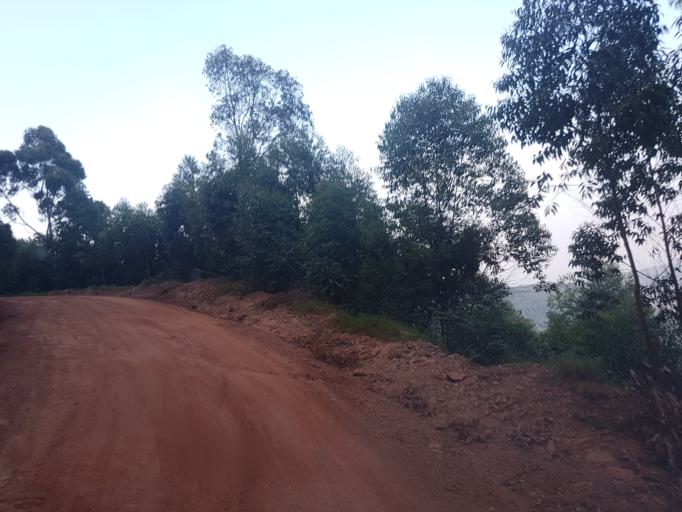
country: UG
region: Western Region
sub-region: Kanungu District
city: Kanungu
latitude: -1.0447
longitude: 29.8834
